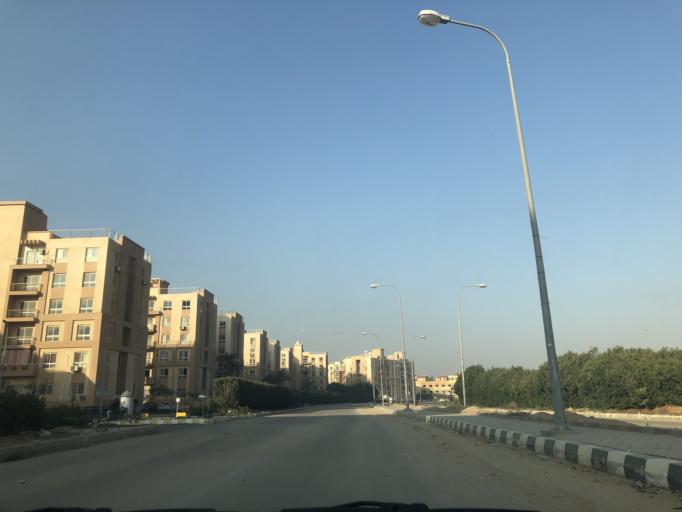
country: EG
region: Al Jizah
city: Madinat Sittah Uktubar
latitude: 29.9088
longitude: 31.0573
